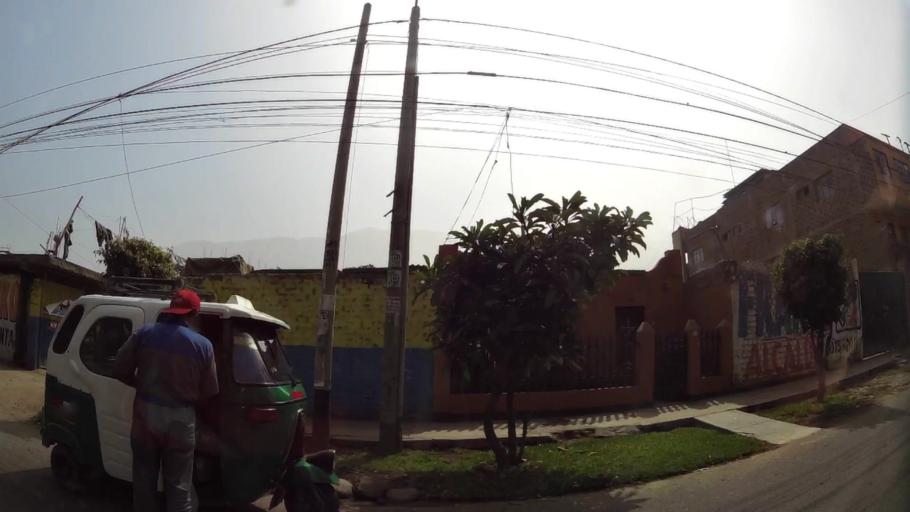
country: PE
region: Lima
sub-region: Lima
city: Asentamiento Humano Nicolas de Pierola
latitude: -11.9398
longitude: -76.6950
